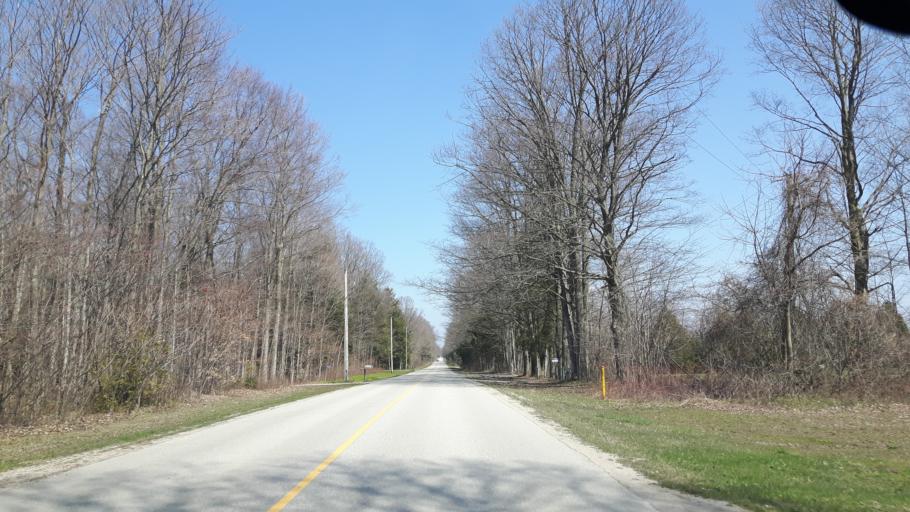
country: CA
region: Ontario
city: Bluewater
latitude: 43.5906
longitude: -81.6848
